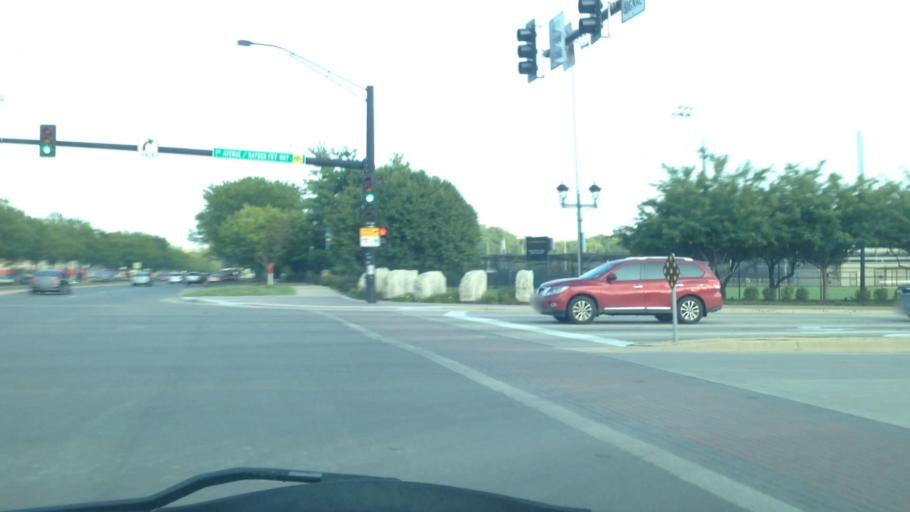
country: US
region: Iowa
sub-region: Johnson County
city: Coralville
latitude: 41.6690
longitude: -91.5661
